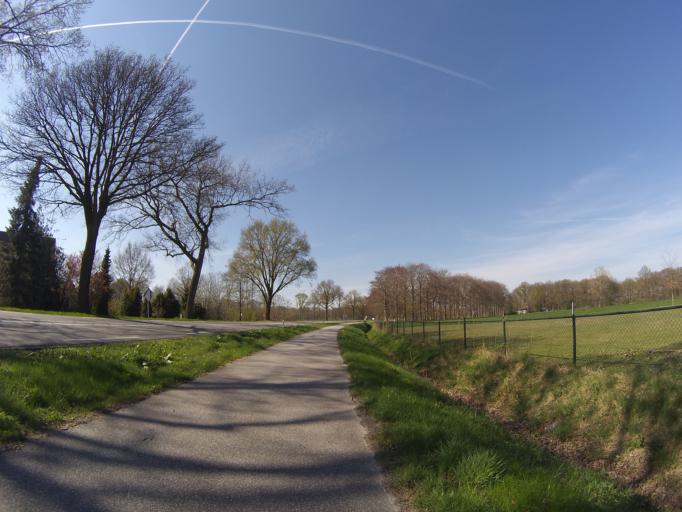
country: NL
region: Gelderland
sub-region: Gemeente Ede
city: Ederveen
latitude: 52.0631
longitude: 5.5542
